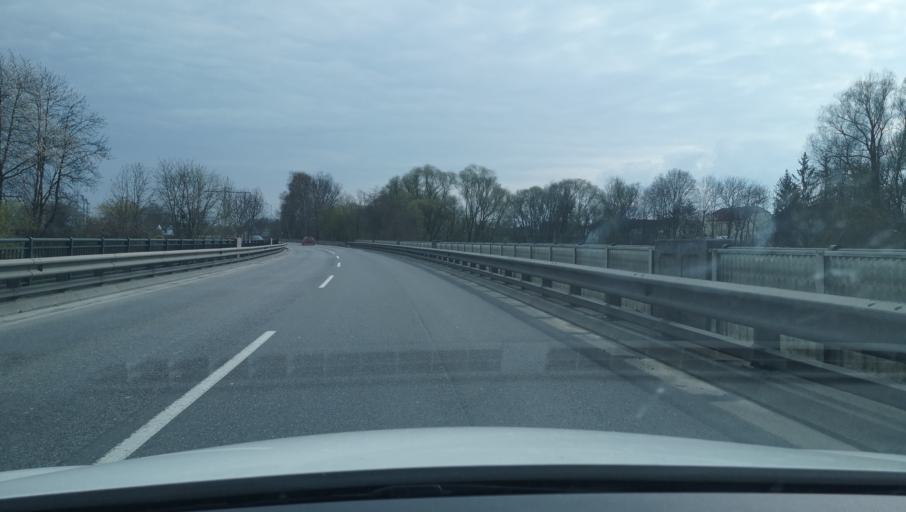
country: AT
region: Lower Austria
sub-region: Politischer Bezirk Amstetten
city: Amstetten
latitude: 48.1137
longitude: 14.8686
